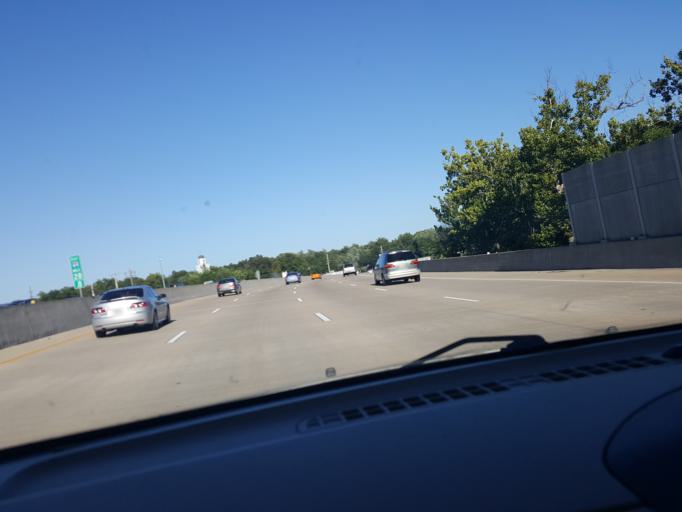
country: US
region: Missouri
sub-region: Saint Louis County
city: Frontenac
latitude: 38.6362
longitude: -90.3956
